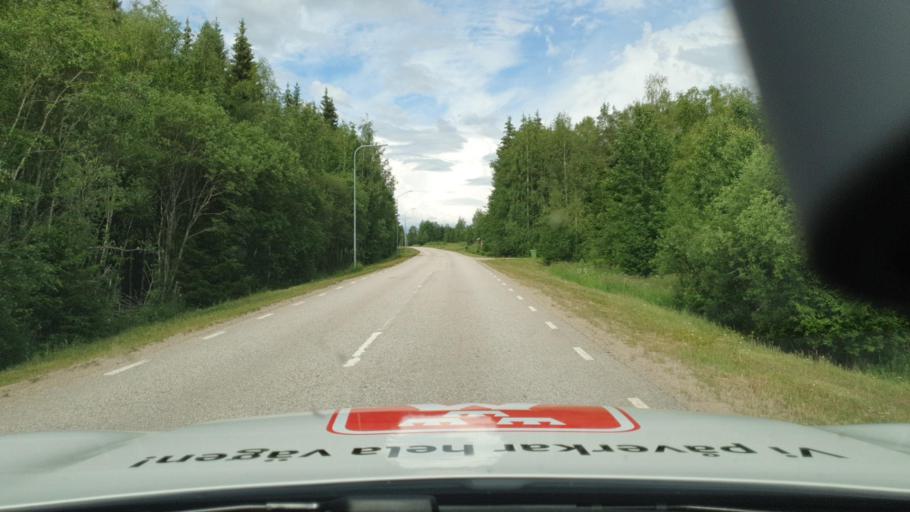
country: NO
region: Hedmark
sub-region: Trysil
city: Innbygda
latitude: 60.9673
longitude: 12.4858
